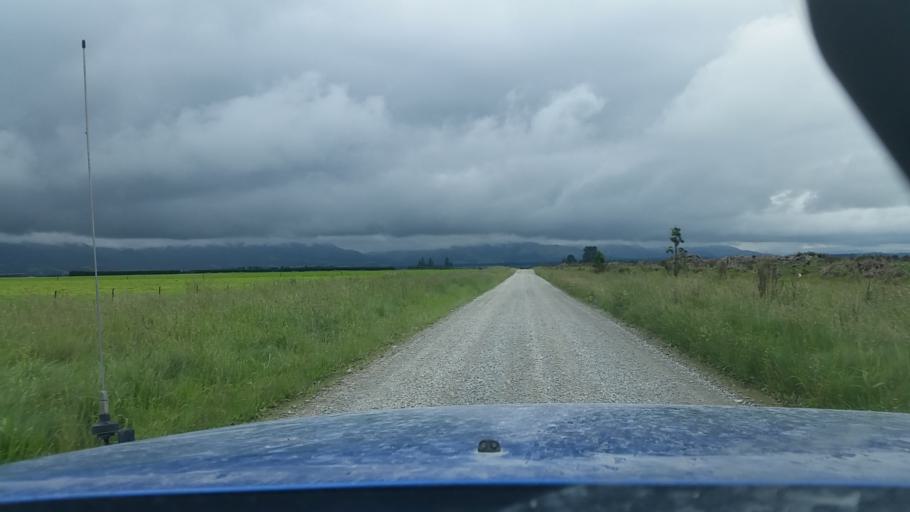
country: NZ
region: Canterbury
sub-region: Ashburton District
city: Methven
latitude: -43.7099
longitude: 171.4590
